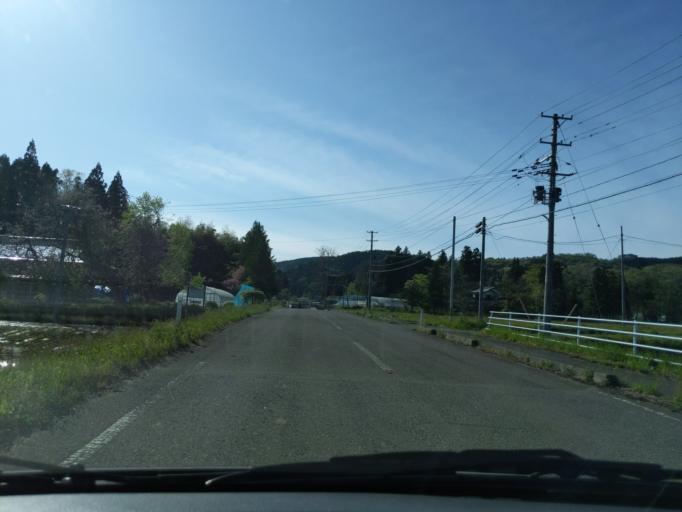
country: JP
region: Iwate
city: Ichinoseki
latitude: 38.8745
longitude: 140.8955
